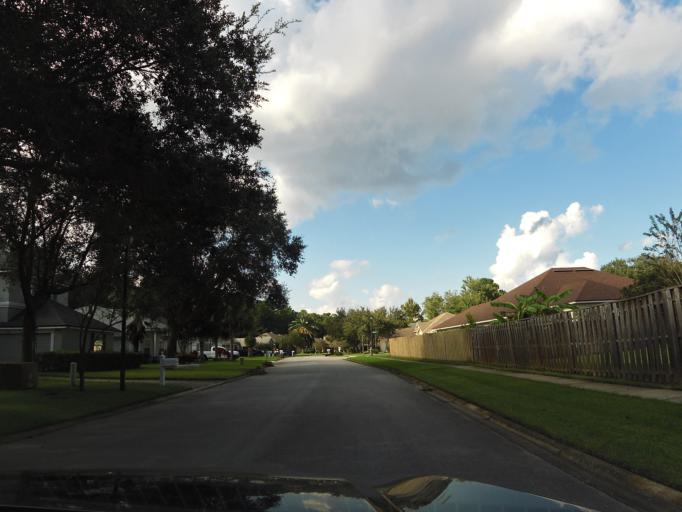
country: US
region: Florida
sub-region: Duval County
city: Jacksonville Beach
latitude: 30.2738
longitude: -81.4981
